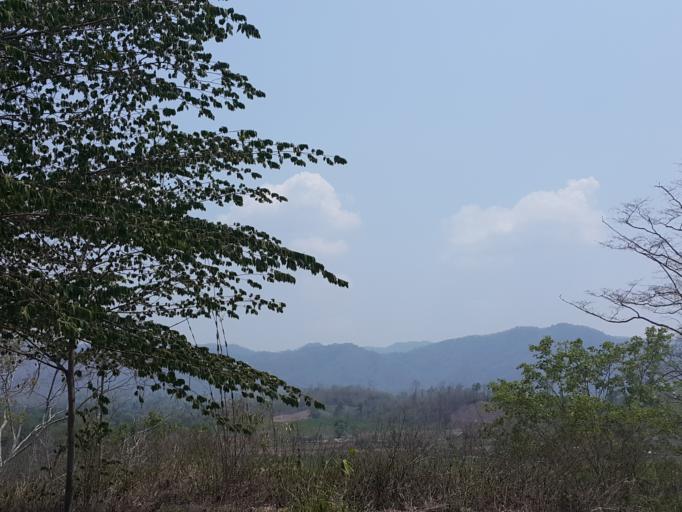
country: TH
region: Kanchanaburi
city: Sai Yok
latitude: 14.1866
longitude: 98.9579
